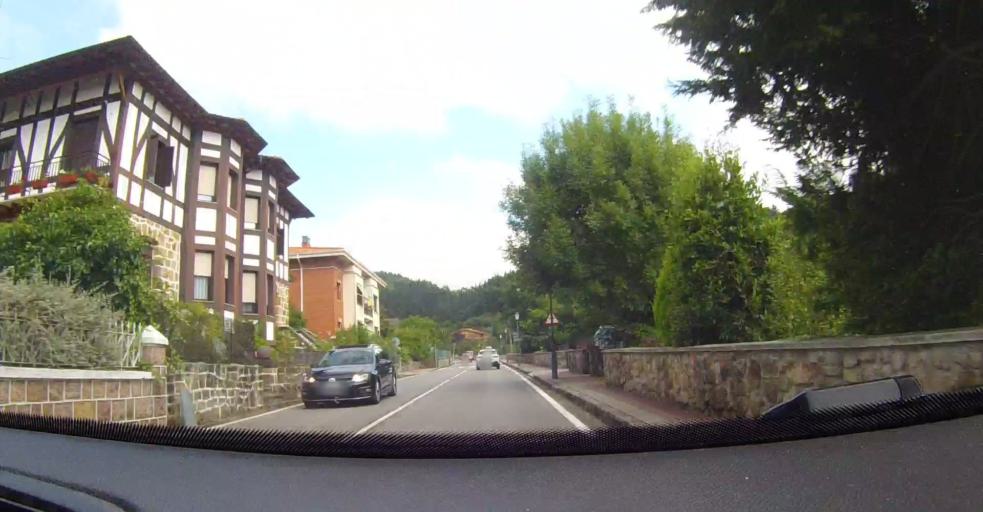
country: ES
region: Basque Country
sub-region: Bizkaia
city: Ibarrangelu
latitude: 43.3893
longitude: -2.6326
